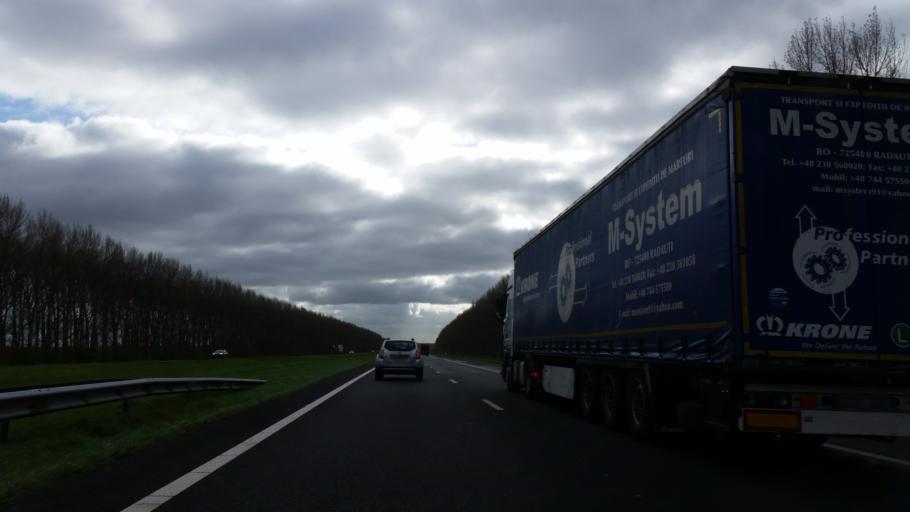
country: NL
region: Flevoland
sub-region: Gemeente Lelystad
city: Lelystad
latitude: 52.5301
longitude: 5.5326
